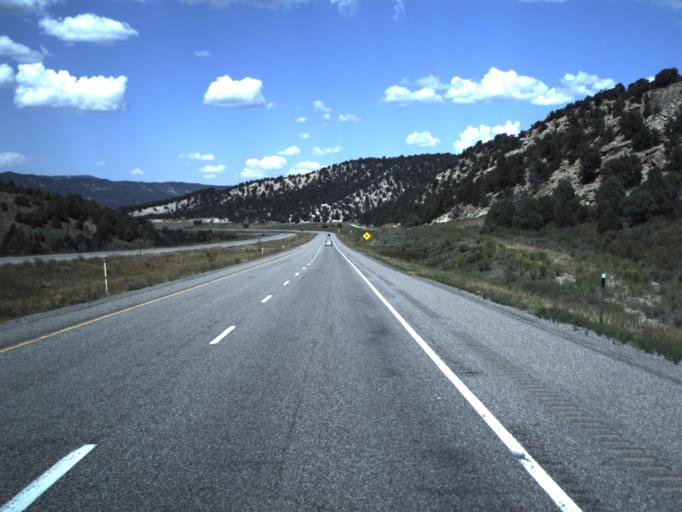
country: US
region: Utah
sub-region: Sevier County
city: Salina
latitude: 38.8413
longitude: -111.5380
